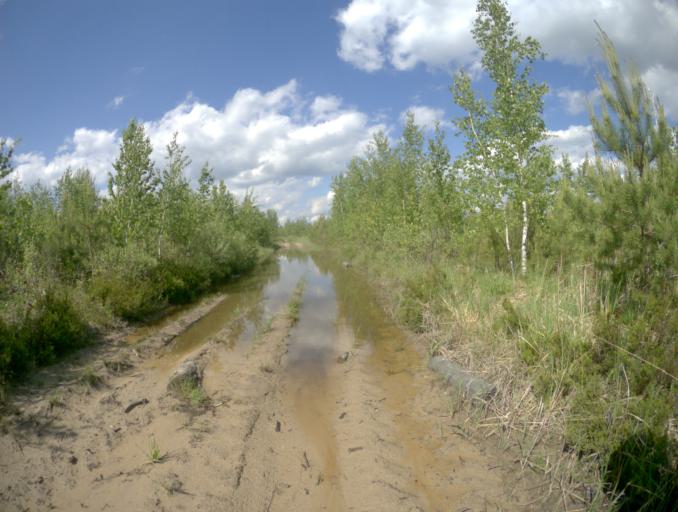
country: RU
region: Vladimir
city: Velikodvorskiy
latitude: 55.2921
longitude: 40.8934
